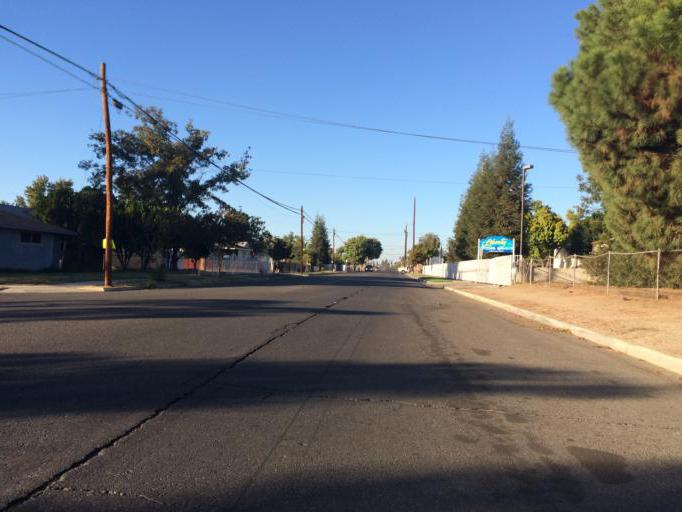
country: US
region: California
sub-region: Fresno County
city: Fresno
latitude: 36.7622
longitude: -119.7635
